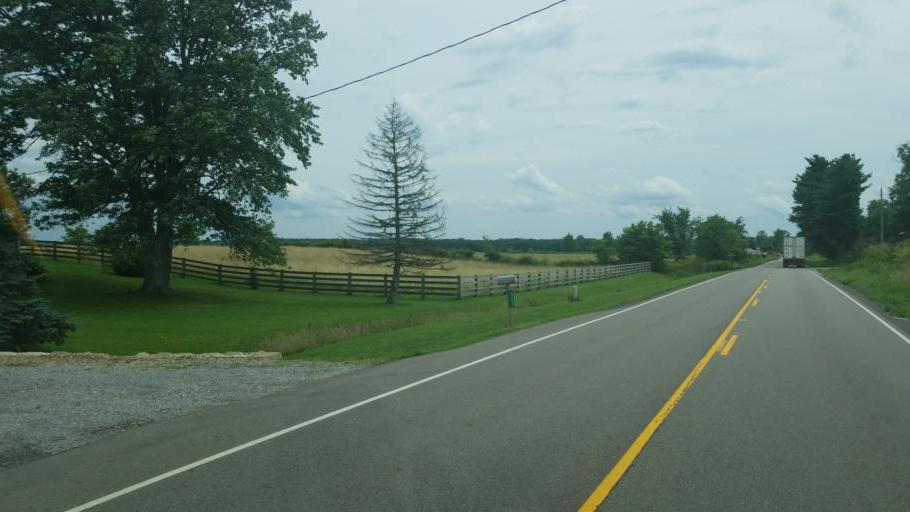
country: US
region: Ohio
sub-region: Licking County
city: Utica
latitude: 40.2900
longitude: -82.5135
